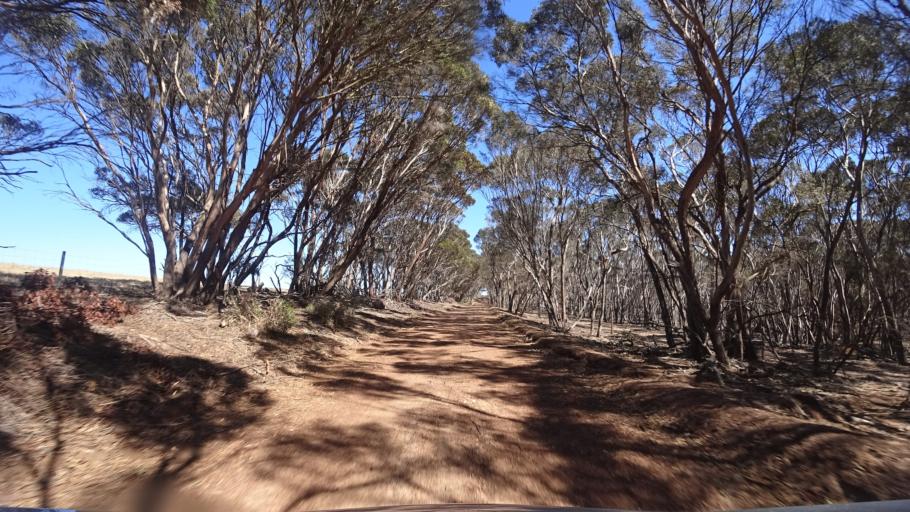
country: AU
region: South Australia
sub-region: Kangaroo Island
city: Kingscote
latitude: -35.7470
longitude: 137.7248
